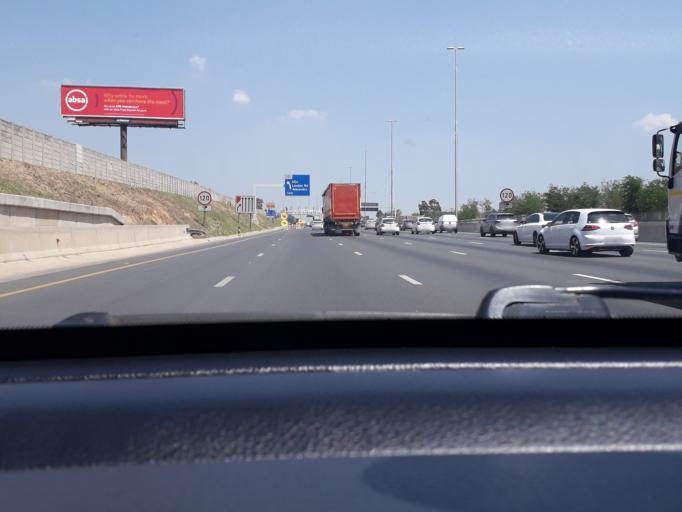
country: ZA
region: Gauteng
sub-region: City of Johannesburg Metropolitan Municipality
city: Modderfontein
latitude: -26.0886
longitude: 28.1161
